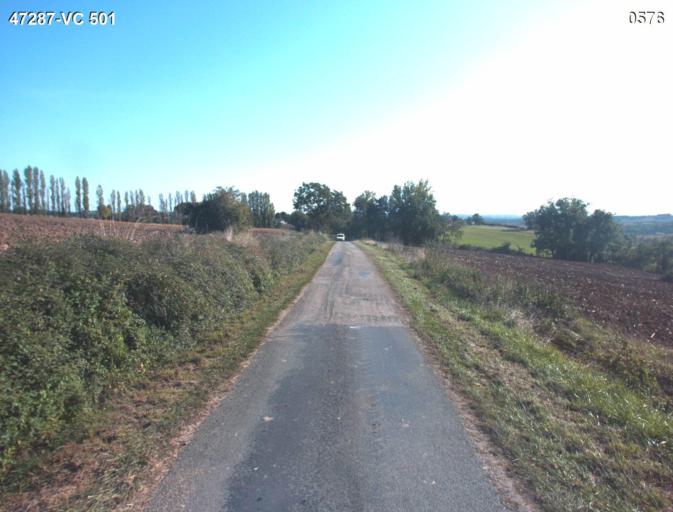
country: FR
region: Aquitaine
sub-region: Departement du Lot-et-Garonne
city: Laplume
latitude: 44.1153
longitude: 0.4598
